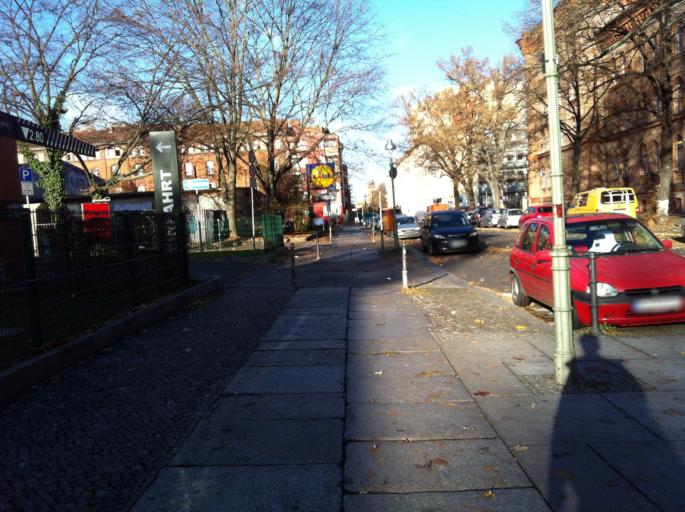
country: DE
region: Berlin
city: Berlin Treptow
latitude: 52.5008
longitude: 13.4363
